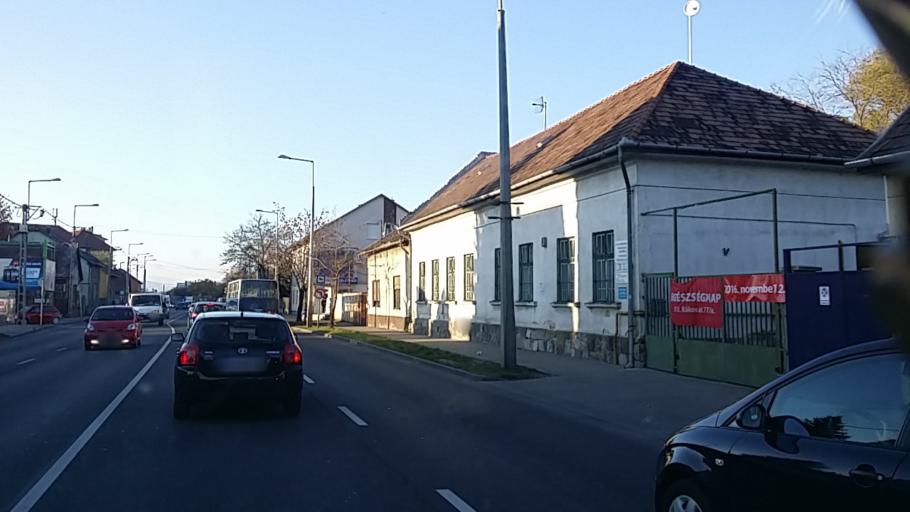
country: HU
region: Budapest
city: Budapest XV. keruelet
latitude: 47.5587
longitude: 19.1234
